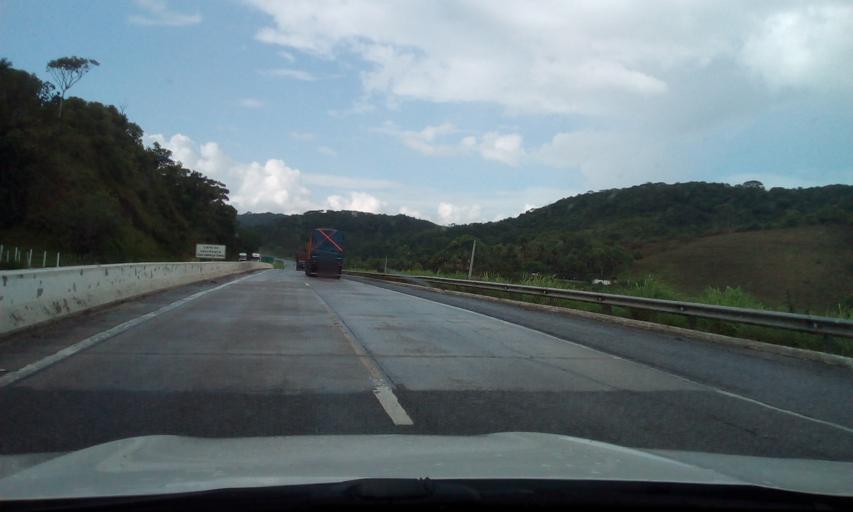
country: BR
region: Pernambuco
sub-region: Cabo De Santo Agostinho
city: Cabo
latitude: -8.3180
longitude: -35.1088
